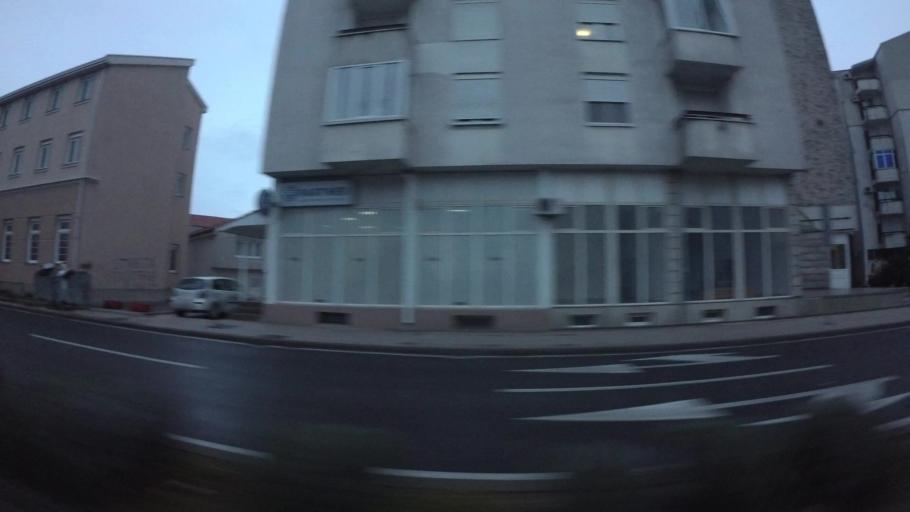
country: BA
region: Federation of Bosnia and Herzegovina
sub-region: Hercegovacko-Bosanski Kanton
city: Mostar
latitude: 43.3387
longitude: 17.8095
